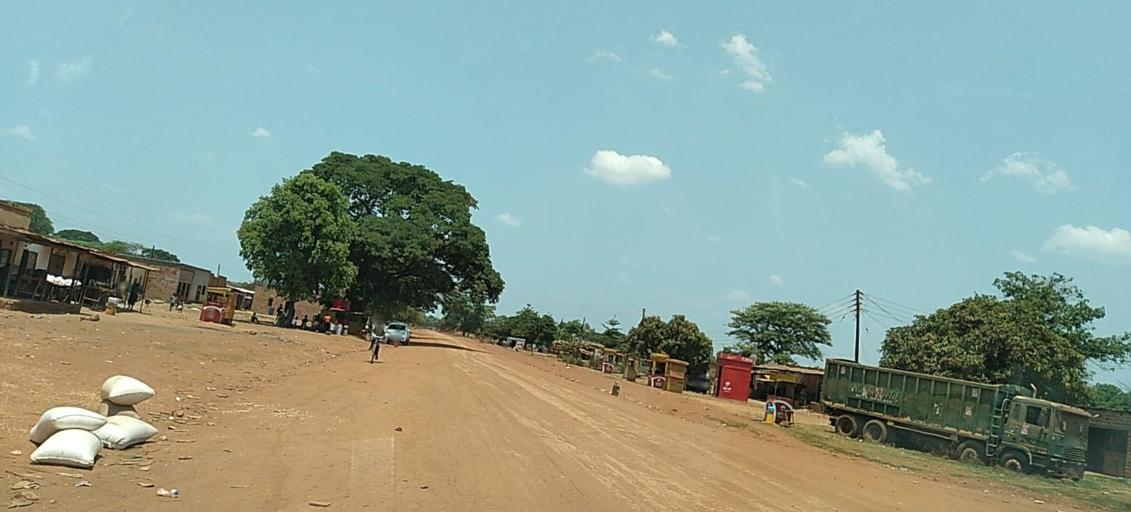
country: ZM
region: Copperbelt
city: Mpongwe
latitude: -13.5136
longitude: 28.0354
